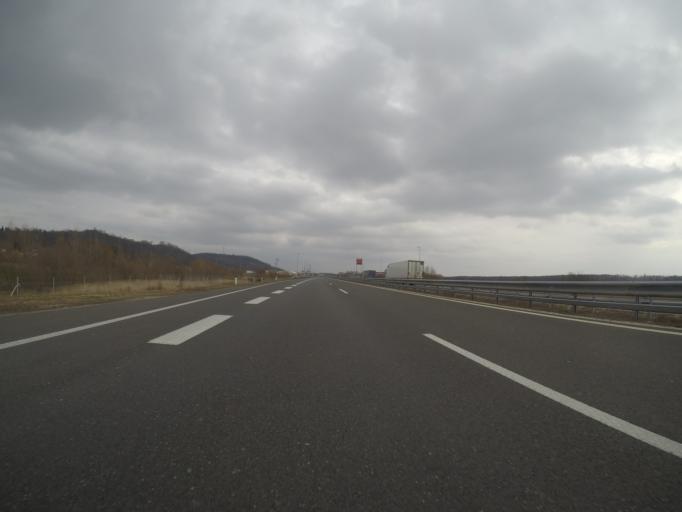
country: HR
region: Medimurska
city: Peklenica
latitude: 46.5236
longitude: 16.5145
